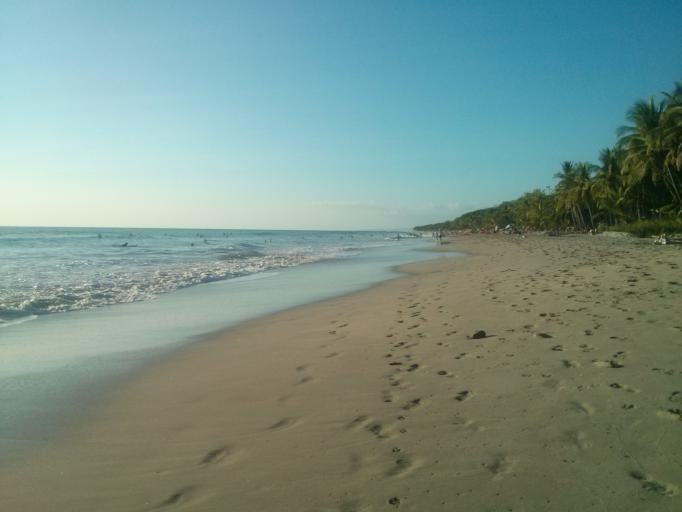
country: CR
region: Guanacaste
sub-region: Canton de Nandayure
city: Bejuco
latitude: 9.6252
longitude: -85.1508
